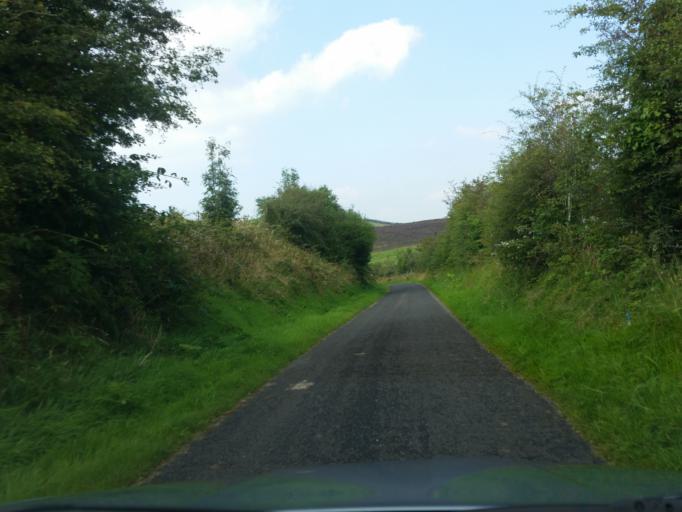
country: GB
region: Northern Ireland
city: Ballinamallard
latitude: 54.3504
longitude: -7.5198
